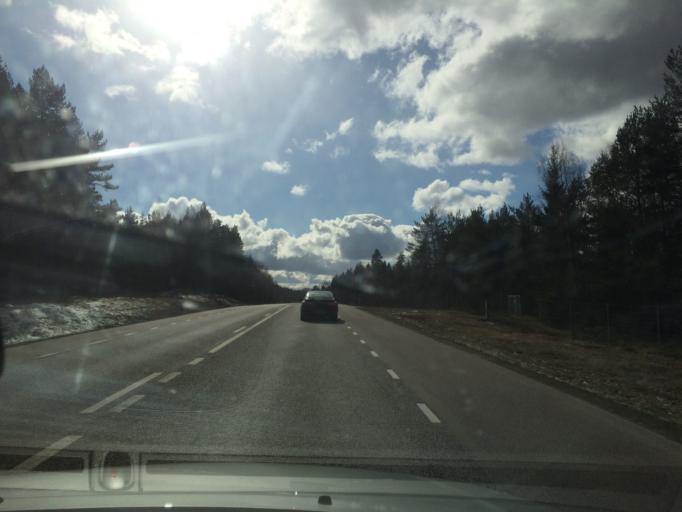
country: SE
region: Vaestra Goetaland
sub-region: Gotene Kommun
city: Goetene
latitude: 58.6000
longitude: 13.6375
